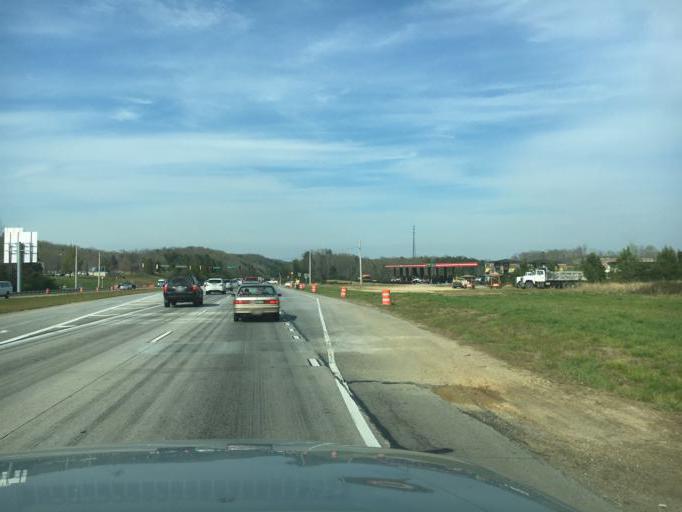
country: US
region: Georgia
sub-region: Hall County
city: Gainesville
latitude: 34.3300
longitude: -83.7833
